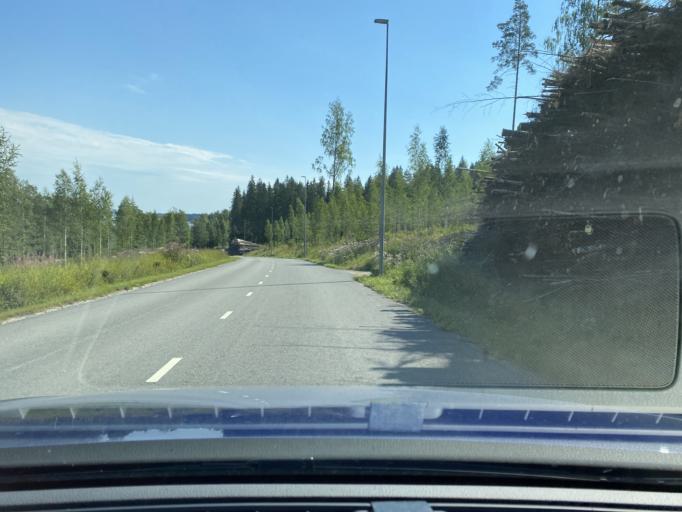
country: FI
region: Central Finland
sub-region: Jyvaeskylae
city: Korpilahti
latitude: 61.8895
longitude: 25.3925
